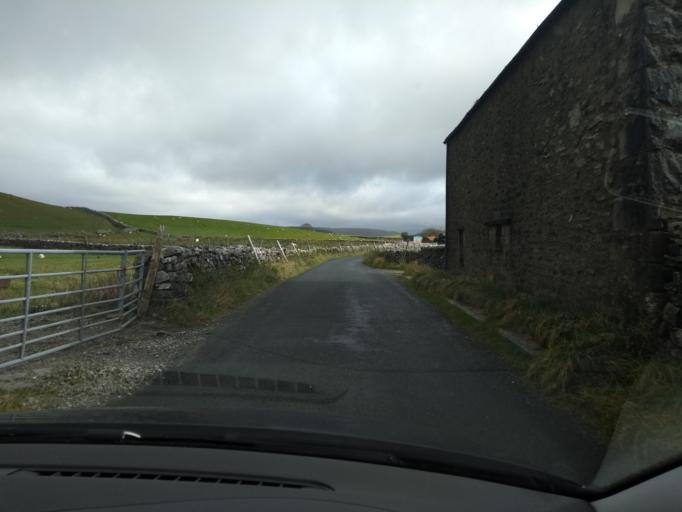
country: GB
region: England
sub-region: North Yorkshire
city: Settle
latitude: 54.0959
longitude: -2.1993
